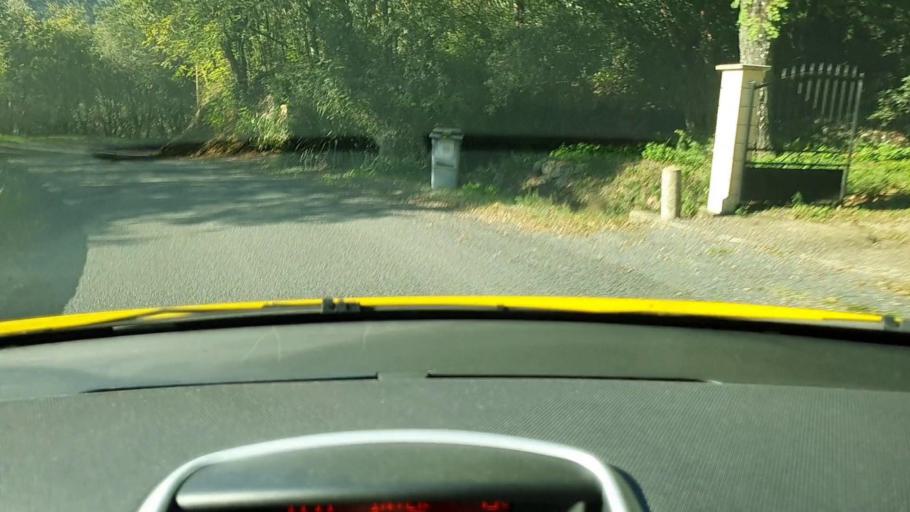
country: FR
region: Languedoc-Roussillon
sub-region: Departement du Gard
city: Valleraugue
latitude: 44.0377
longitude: 3.6803
